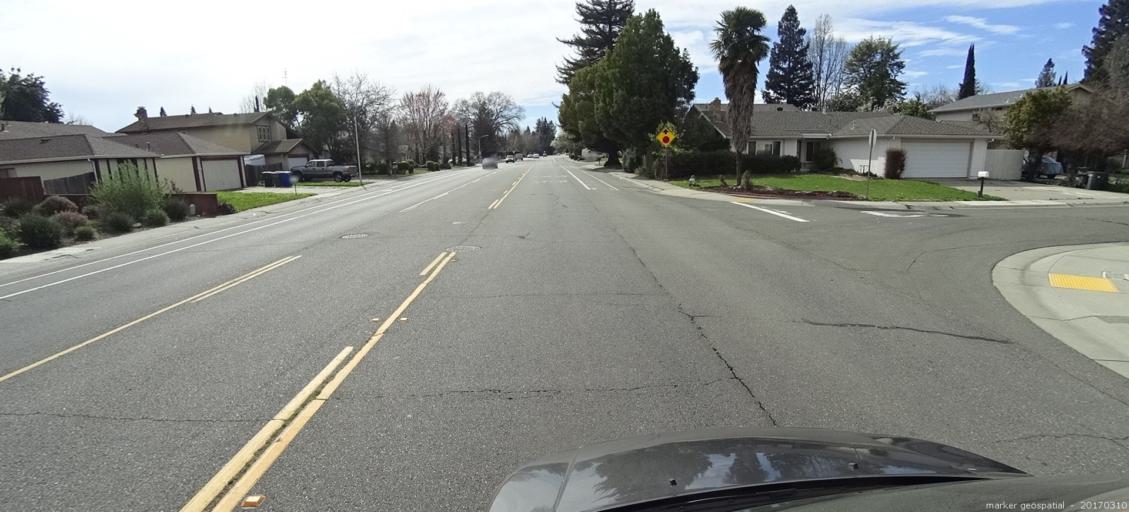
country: US
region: California
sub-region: Sacramento County
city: Parkway
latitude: 38.4903
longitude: -121.5235
